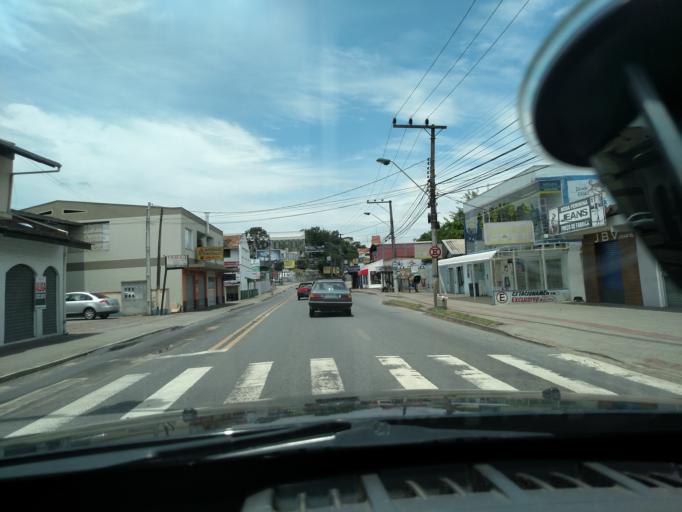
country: BR
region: Santa Catarina
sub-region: Blumenau
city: Blumenau
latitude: -26.8734
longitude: -49.0890
